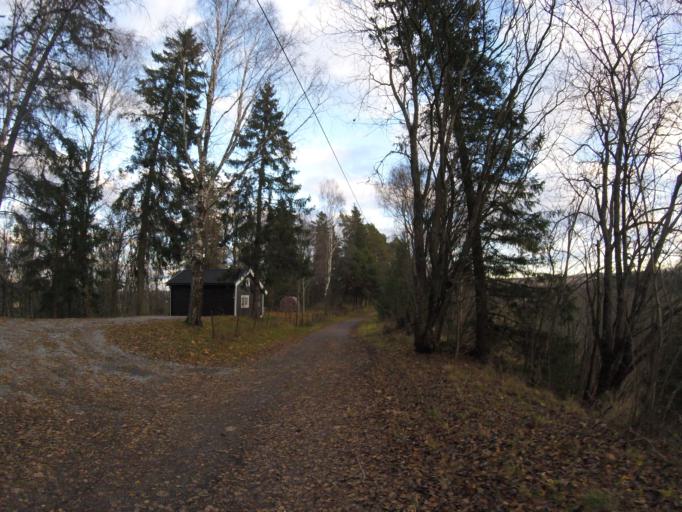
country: NO
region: Akershus
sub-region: Skedsmo
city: Leirsund
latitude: 59.9979
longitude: 11.0726
